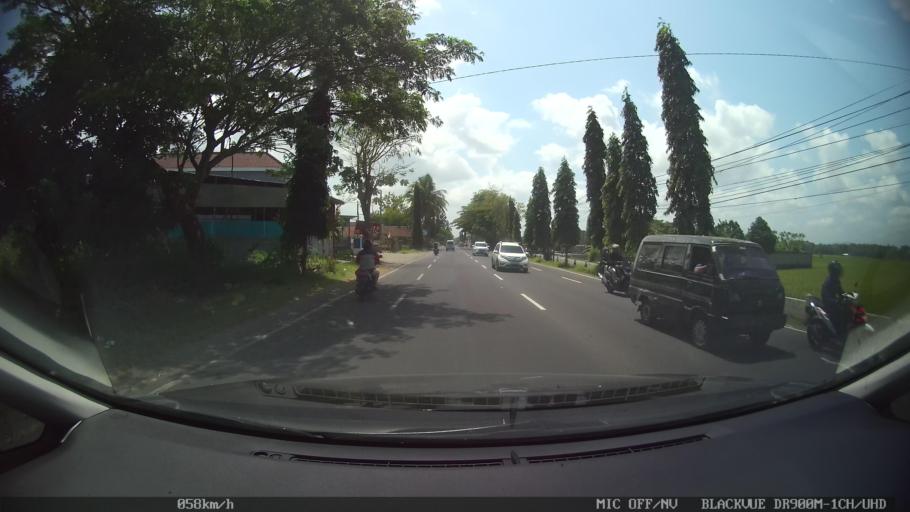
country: ID
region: Daerah Istimewa Yogyakarta
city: Pandak
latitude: -7.9217
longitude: 110.2813
